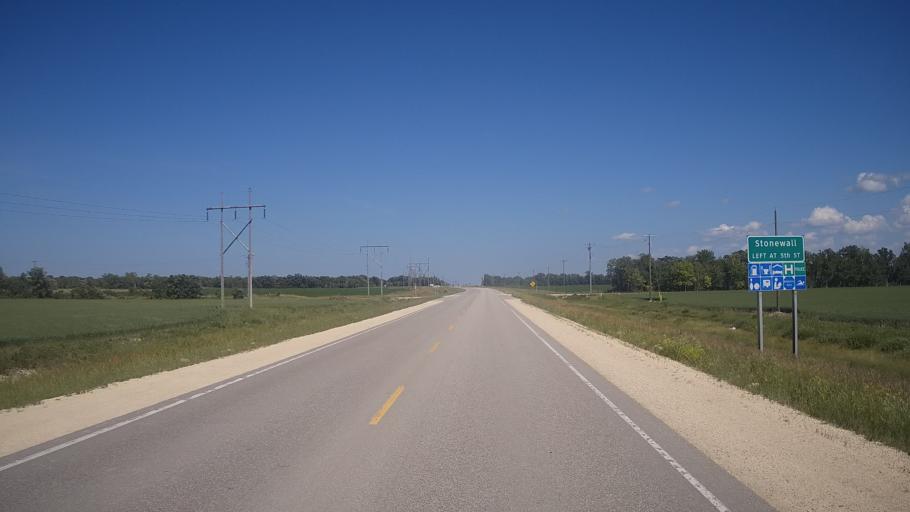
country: CA
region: Manitoba
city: Stonewall
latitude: 50.1228
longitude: -97.3474
